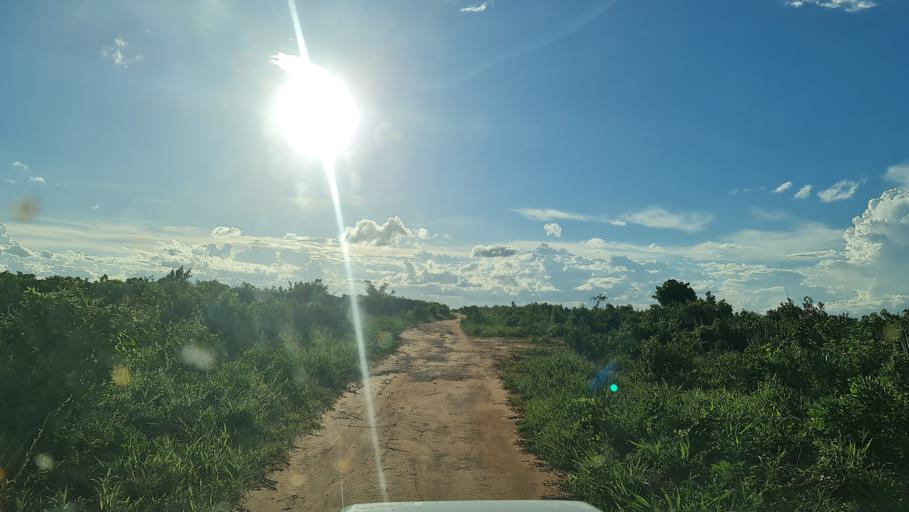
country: MZ
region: Nampula
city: Ilha de Mocambique
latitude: -14.9519
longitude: 40.1758
